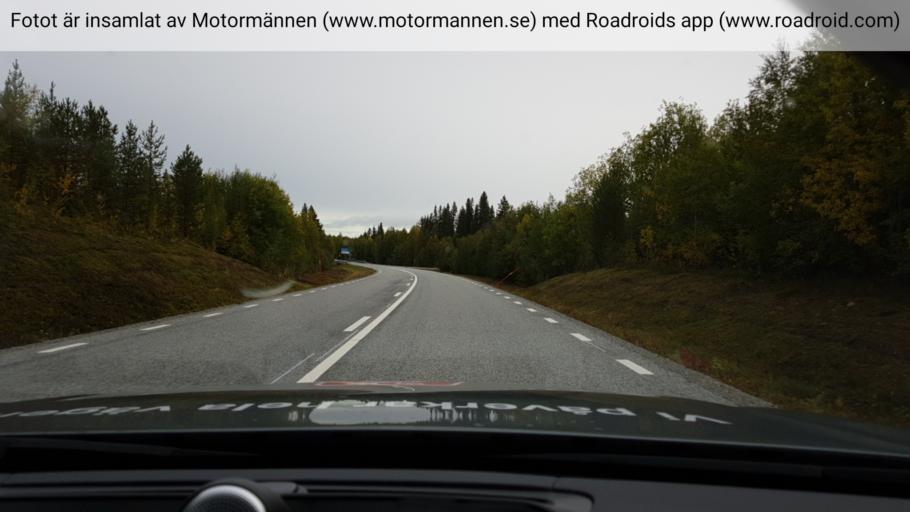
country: SE
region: Jaemtland
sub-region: Stroemsunds Kommun
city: Stroemsund
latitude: 64.1410
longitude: 15.6804
